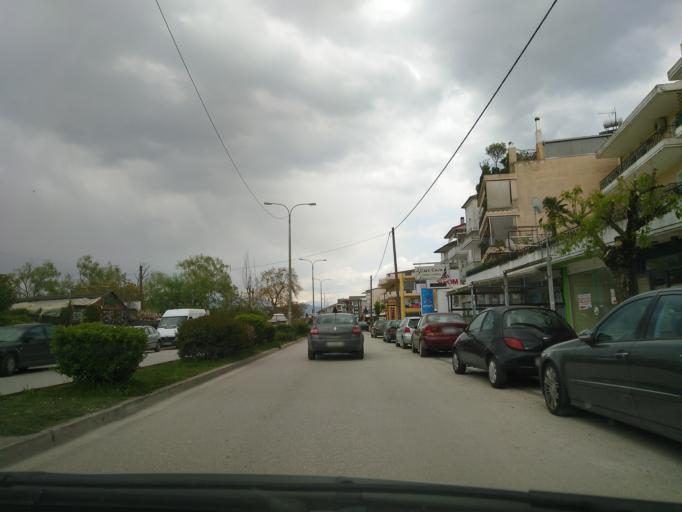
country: GR
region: Epirus
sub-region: Nomos Ioanninon
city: Ioannina
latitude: 39.6737
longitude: 20.8481
